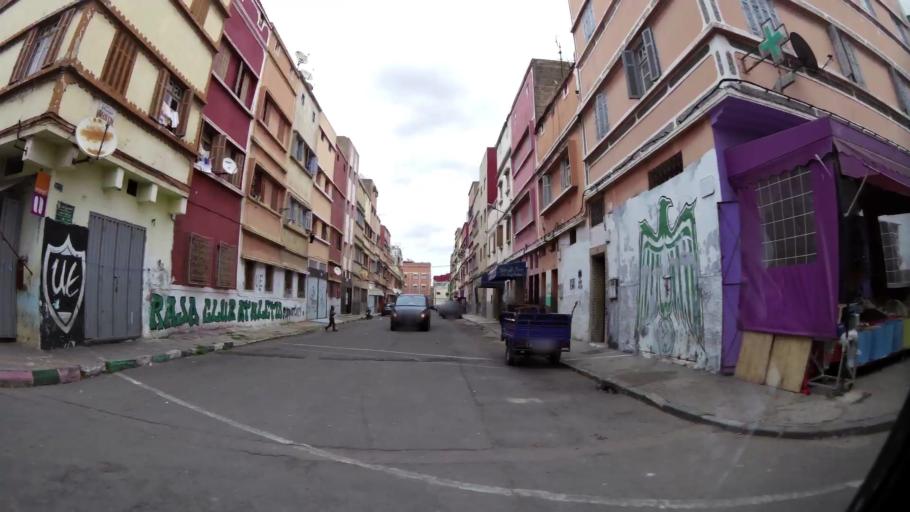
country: MA
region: Grand Casablanca
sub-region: Casablanca
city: Casablanca
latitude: 33.5667
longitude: -7.5676
